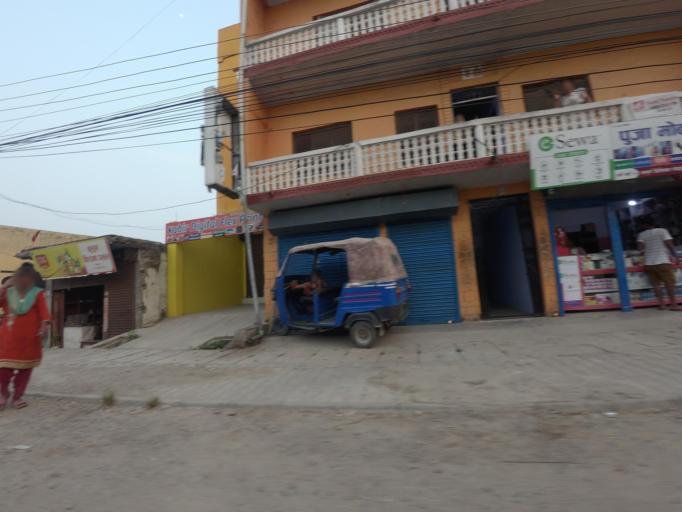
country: NP
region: Western Region
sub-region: Lumbini Zone
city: Bhairahawa
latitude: 27.5059
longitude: 83.4613
